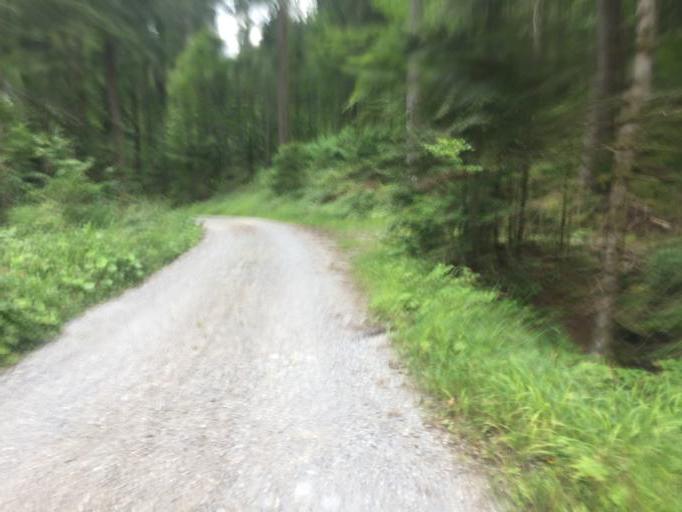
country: CH
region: Bern
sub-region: Thun District
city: Wattenwil
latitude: 46.7551
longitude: 7.4800
